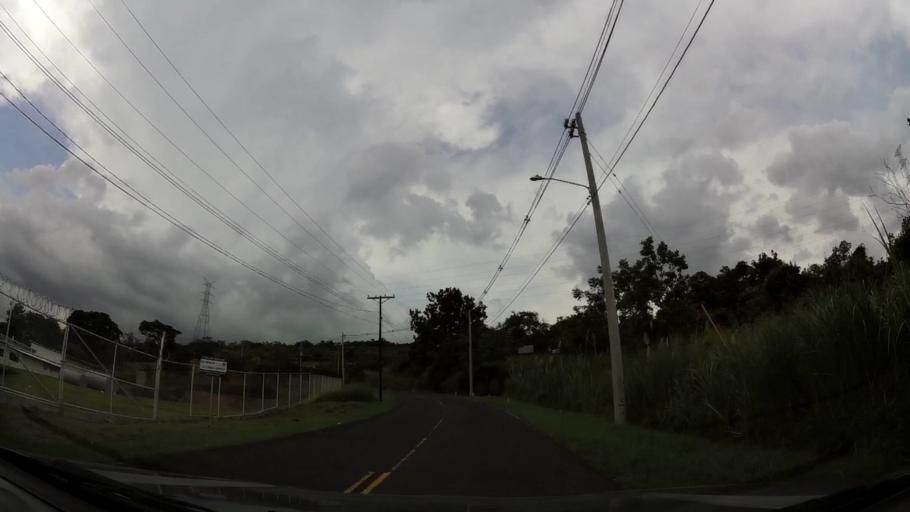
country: PA
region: Panama
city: Cabra Numero Uno
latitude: 9.1250
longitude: -79.3629
